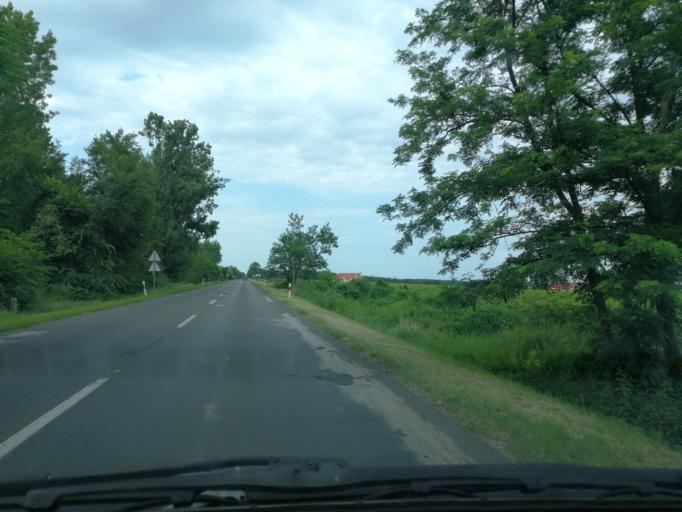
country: HU
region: Bacs-Kiskun
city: Ersekcsanad
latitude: 46.2364
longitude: 18.9763
